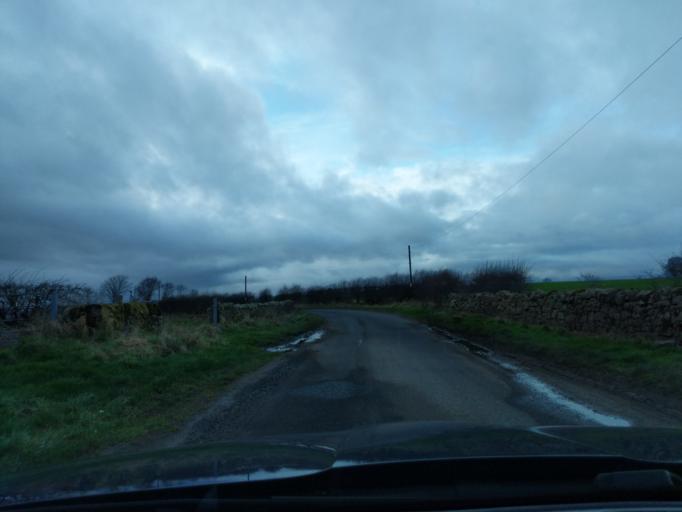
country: GB
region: England
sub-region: Northumberland
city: Ford
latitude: 55.7124
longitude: -2.1109
